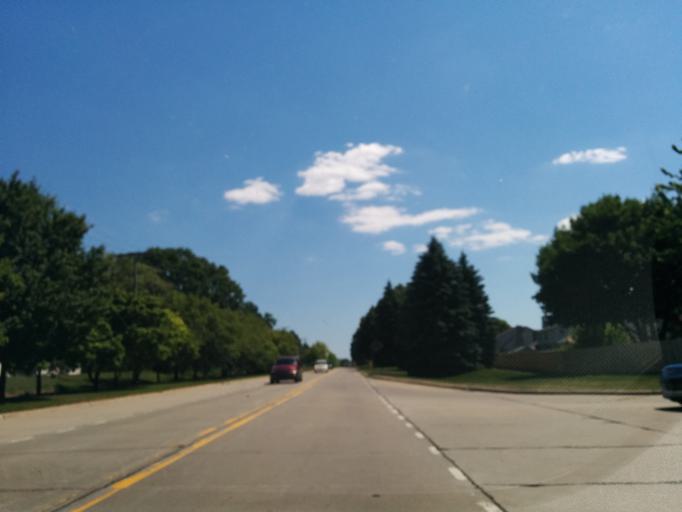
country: US
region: Michigan
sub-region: Oakland County
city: Farmington Hills
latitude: 42.5164
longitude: -83.4182
